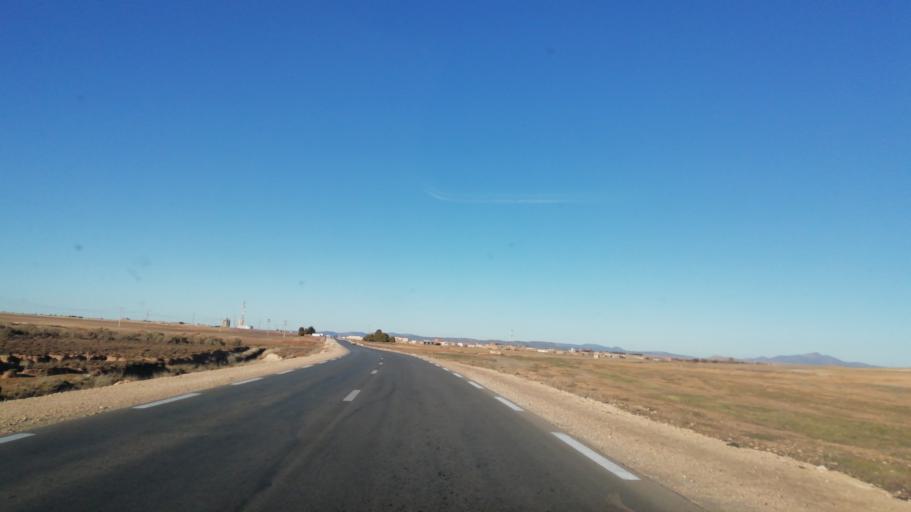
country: DZ
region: Tlemcen
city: Sebdou
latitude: 34.4709
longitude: -1.2722
